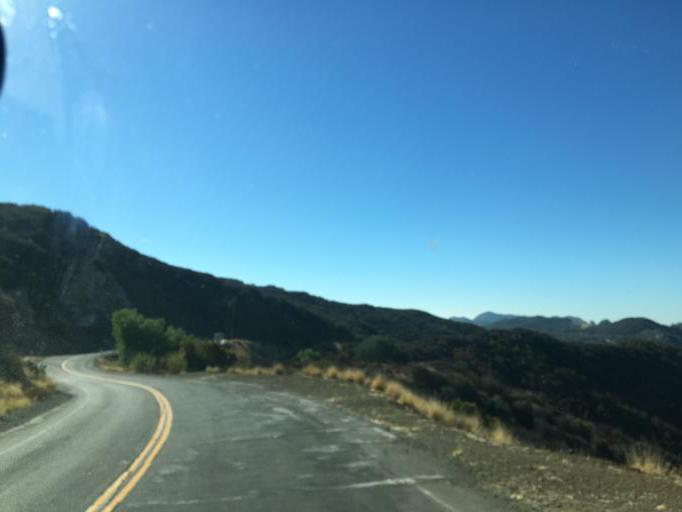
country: US
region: California
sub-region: Ventura County
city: Thousand Oaks
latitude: 34.0979
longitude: -118.8856
